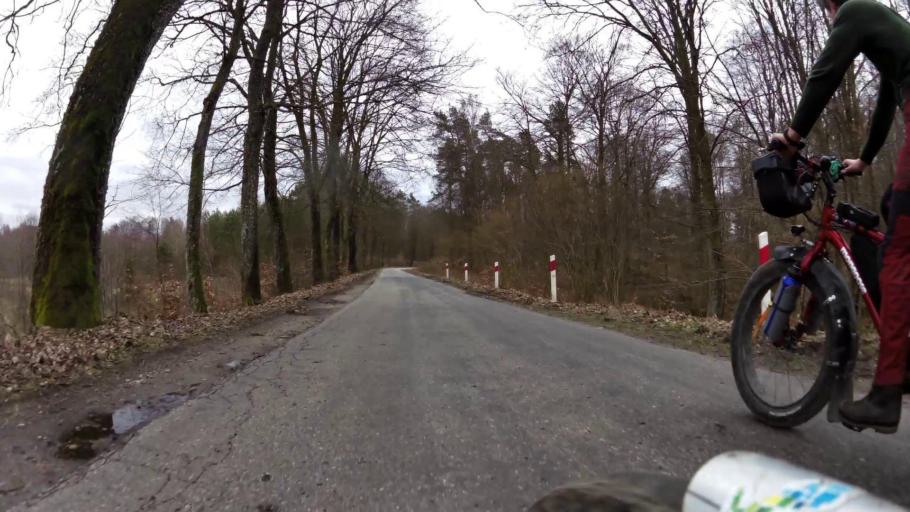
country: PL
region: Pomeranian Voivodeship
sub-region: Powiat bytowski
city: Trzebielino
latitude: 54.0983
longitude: 17.1330
